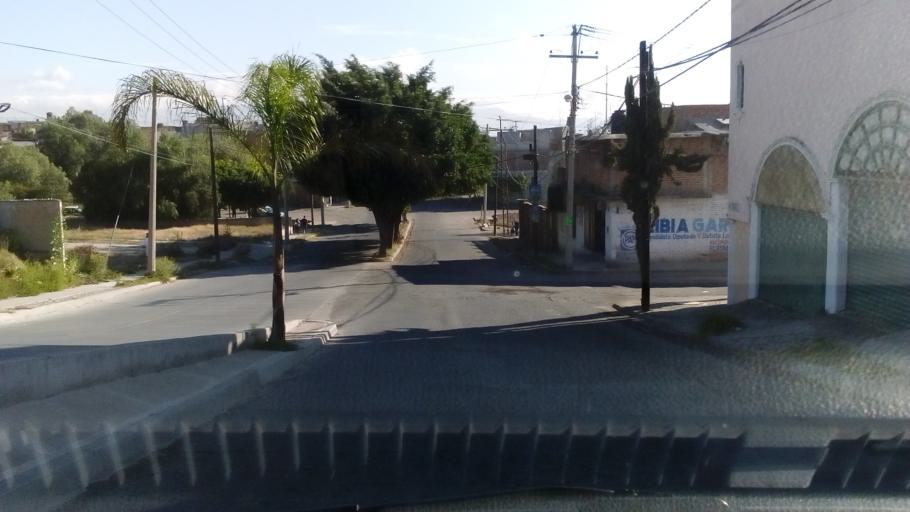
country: MX
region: Guanajuato
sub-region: Leon
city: Ejido la Joya
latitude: 21.1122
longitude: -101.7143
